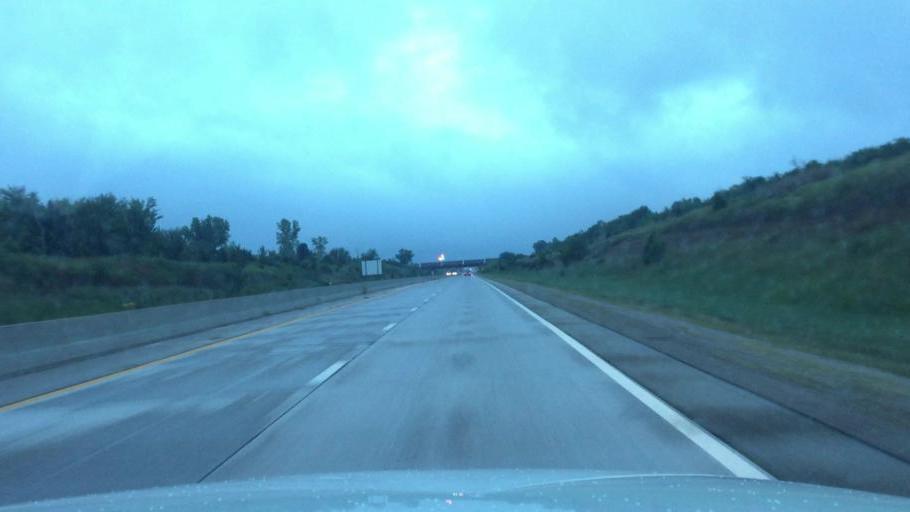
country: US
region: Kansas
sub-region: Neosho County
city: Chanute
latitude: 37.6685
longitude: -95.4796
